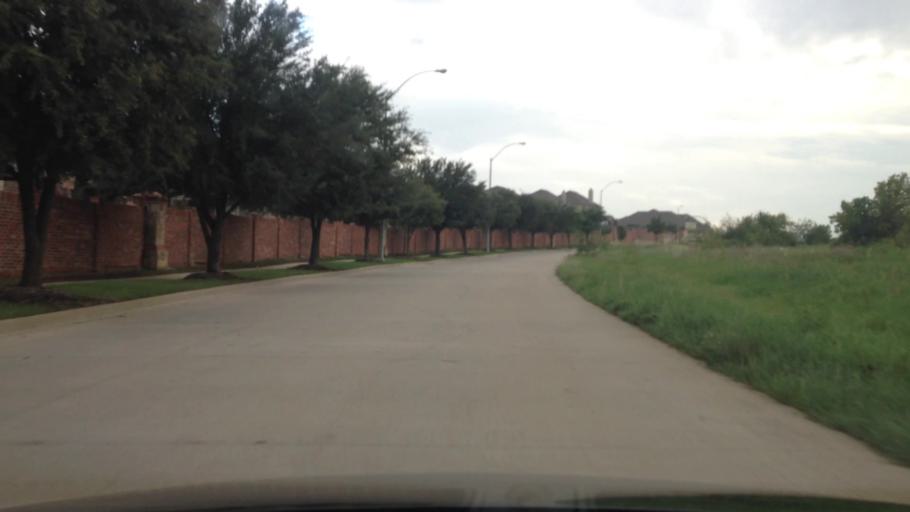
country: US
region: Texas
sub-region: Tarrant County
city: Crowley
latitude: 32.5757
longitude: -97.3291
